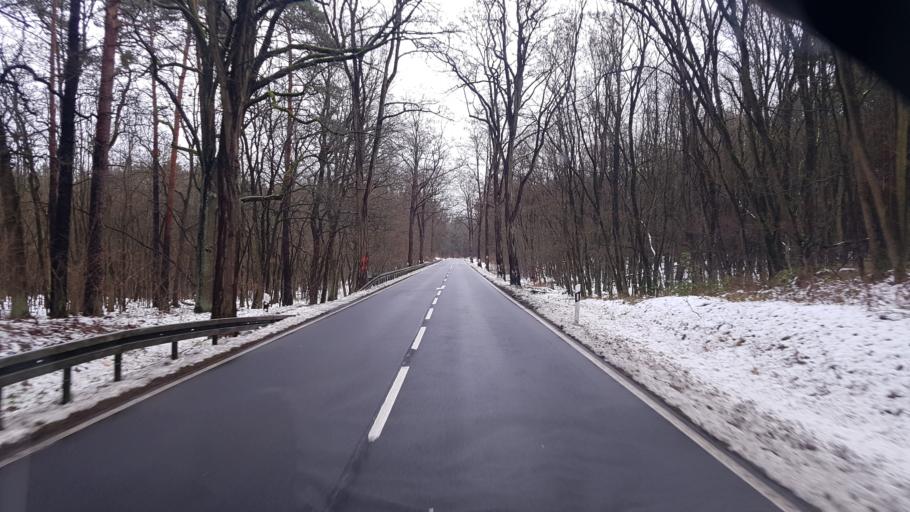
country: DE
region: Brandenburg
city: Schenkendobern
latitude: 51.9750
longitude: 14.5556
